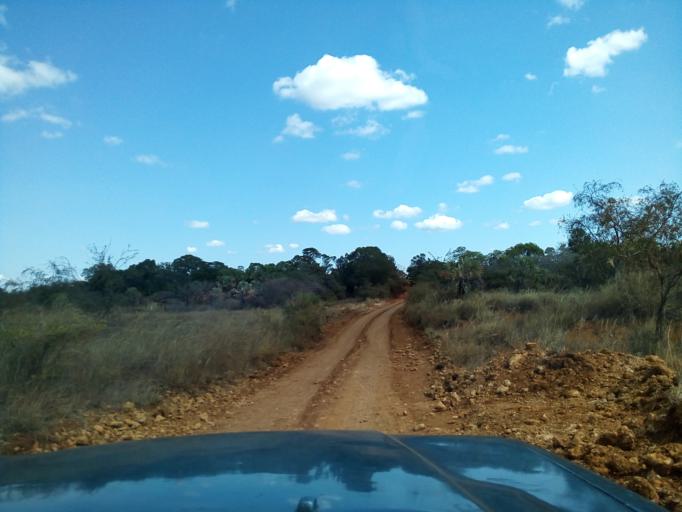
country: MG
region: Boeny
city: Mahajanga
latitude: -15.9715
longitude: 46.0813
